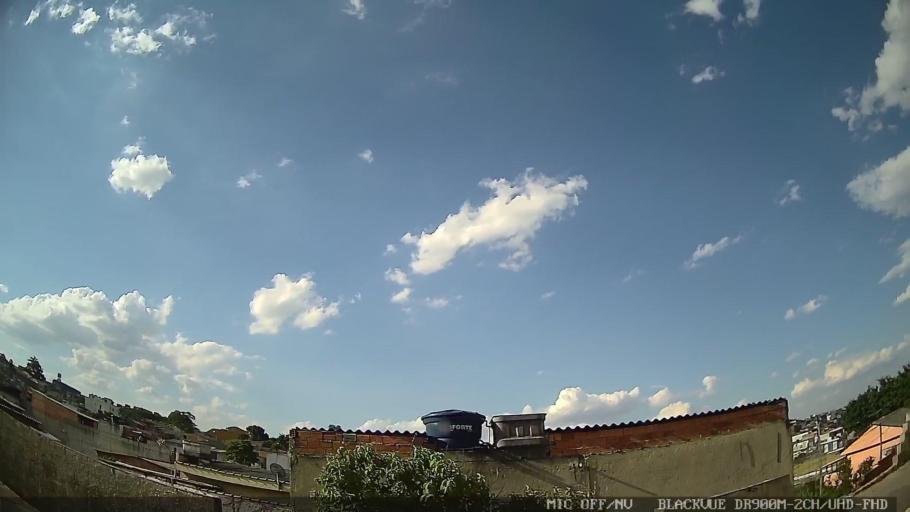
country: BR
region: Sao Paulo
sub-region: Ferraz De Vasconcelos
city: Ferraz de Vasconcelos
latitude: -23.5259
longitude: -46.4382
